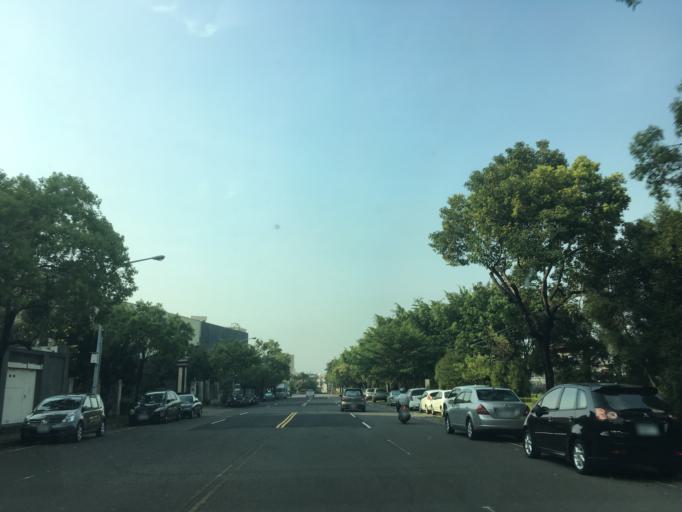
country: TW
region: Taiwan
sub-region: Taichung City
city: Taichung
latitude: 24.0587
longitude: 120.6804
